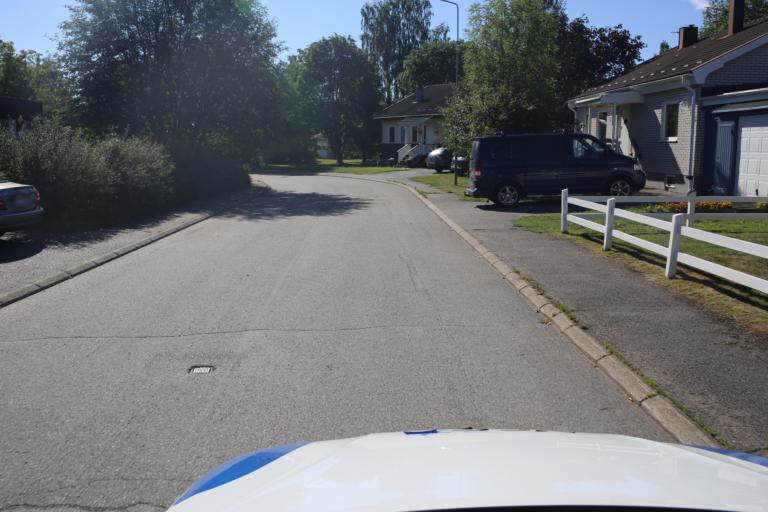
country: SE
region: Vaesterbotten
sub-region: Skelleftea Kommun
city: Viken
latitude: 64.7456
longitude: 20.7660
